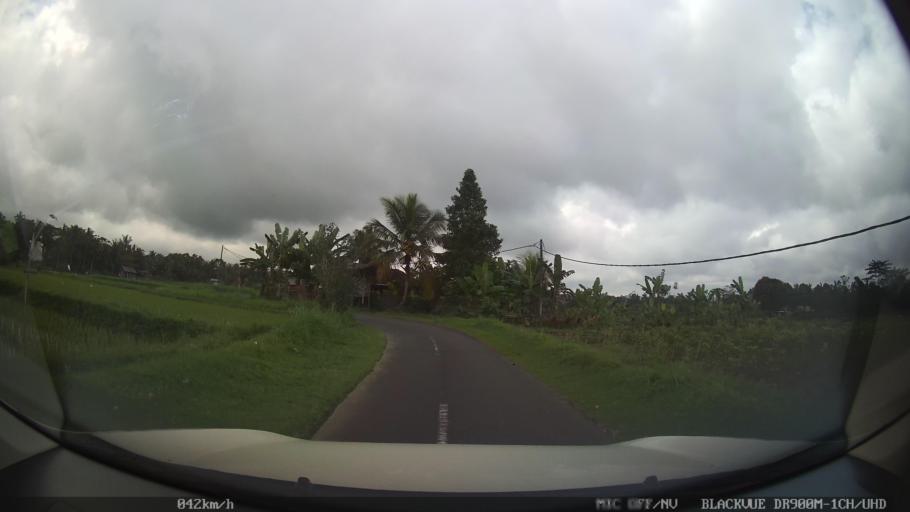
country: ID
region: Bali
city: Badung
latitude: -8.4211
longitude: 115.2273
